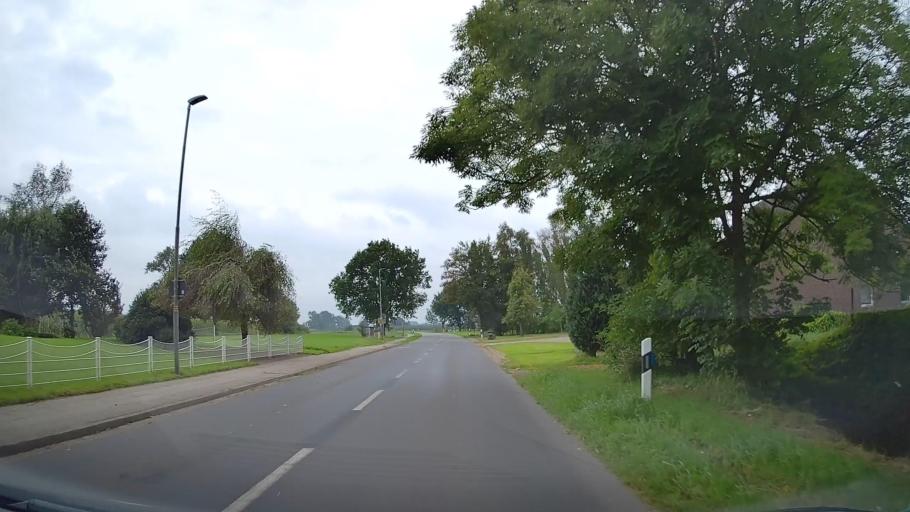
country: DE
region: Lower Saxony
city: Stade
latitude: 53.6342
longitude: 9.4636
